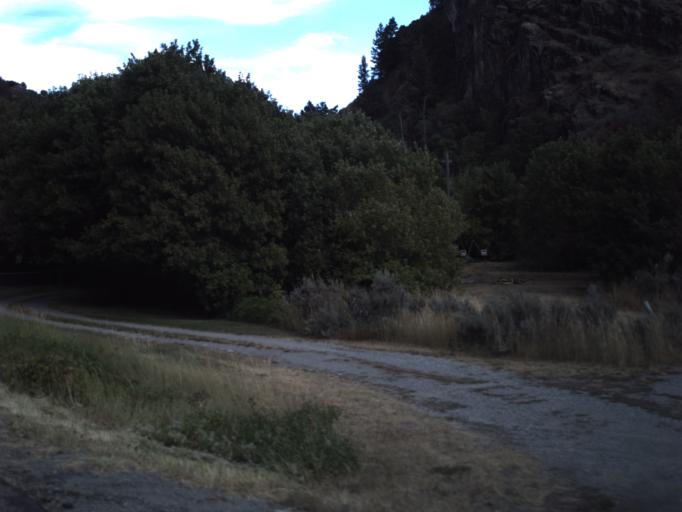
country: US
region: Utah
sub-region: Cache County
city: Millville
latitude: 41.6307
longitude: -111.7104
